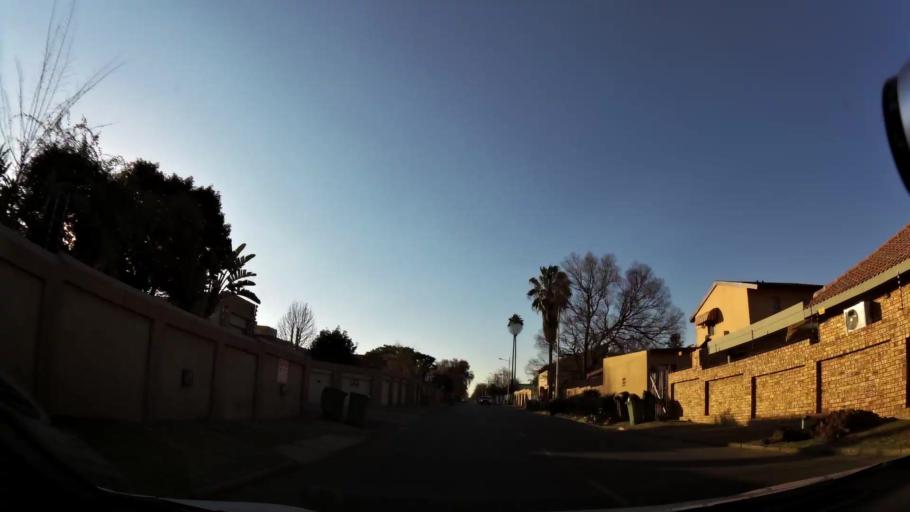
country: ZA
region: Gauteng
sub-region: Ekurhuleni Metropolitan Municipality
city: Germiston
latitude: -26.2723
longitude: 28.1137
